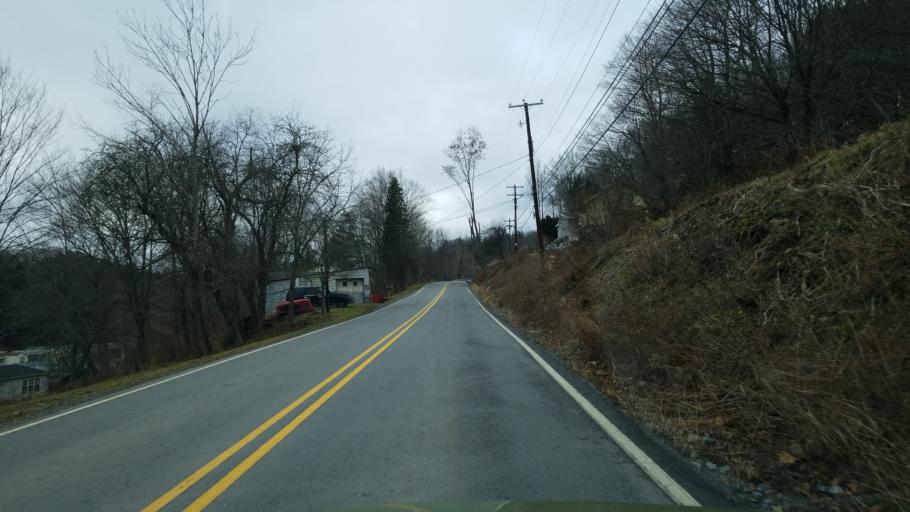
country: US
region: Pennsylvania
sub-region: Clearfield County
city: Clearfield
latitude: 41.0310
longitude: -78.4577
